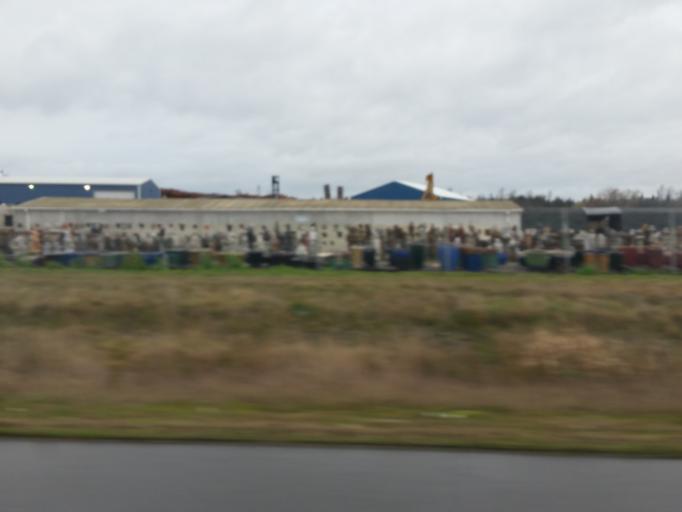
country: US
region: Washington
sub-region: Skagit County
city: Mount Vernon
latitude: 48.4471
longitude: -122.4284
